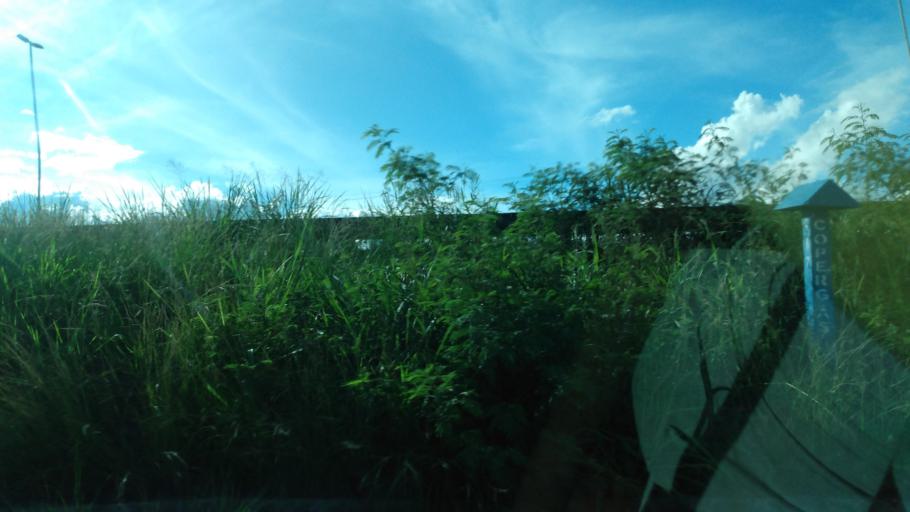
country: ET
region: Oromiya
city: Gore
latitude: 8.1971
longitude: 35.5774
